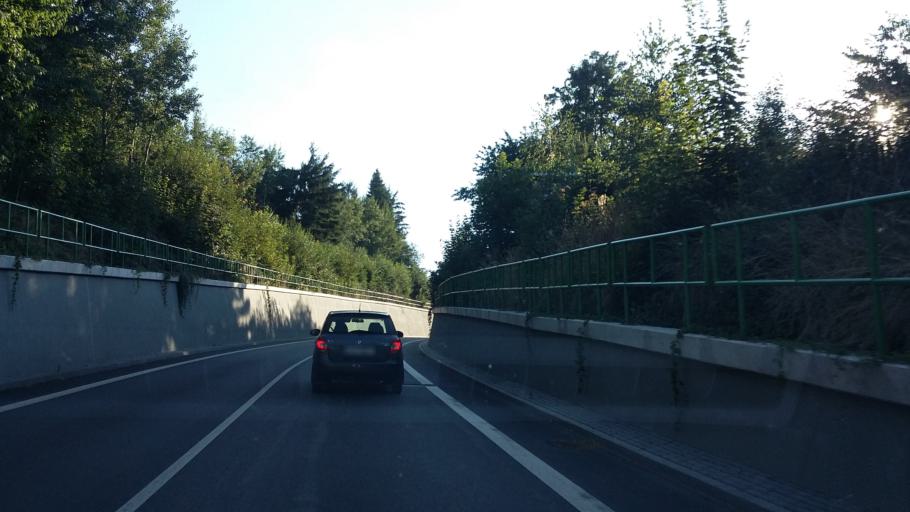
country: CZ
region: Vysocina
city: Kamenice
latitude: 49.3969
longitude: 15.7909
